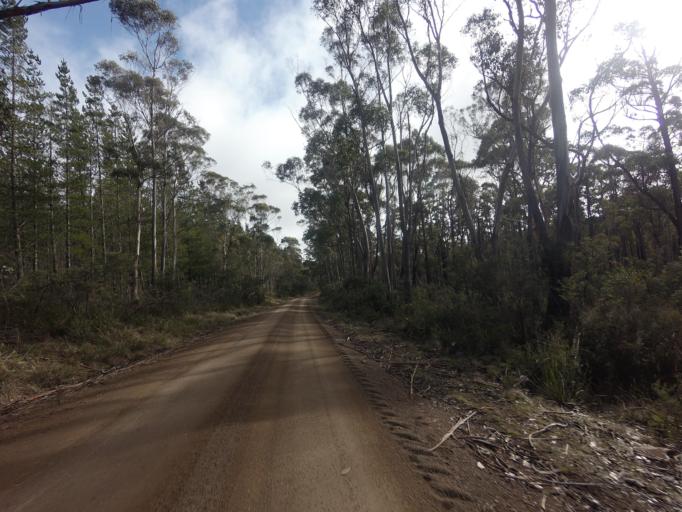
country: AU
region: Tasmania
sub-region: Derwent Valley
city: New Norfolk
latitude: -42.7623
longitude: 146.8951
